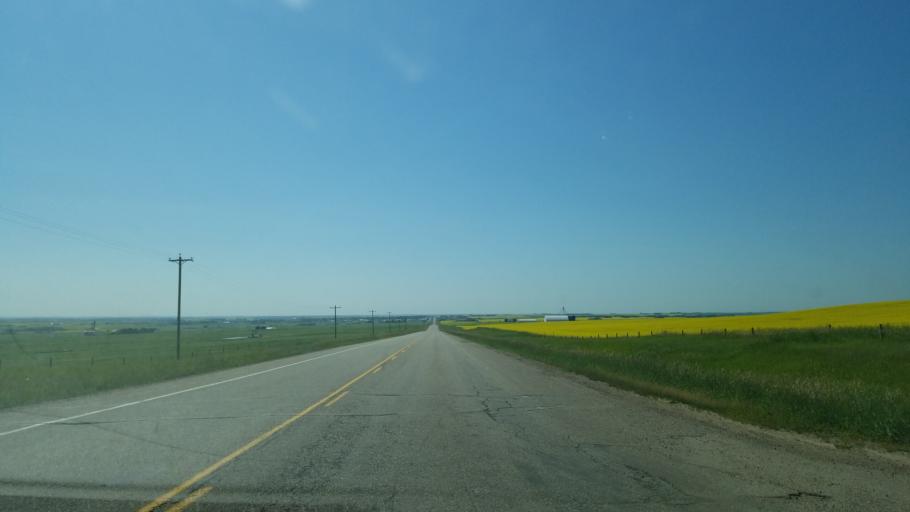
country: CA
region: Alberta
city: Provost
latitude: 52.3612
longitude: -110.1728
